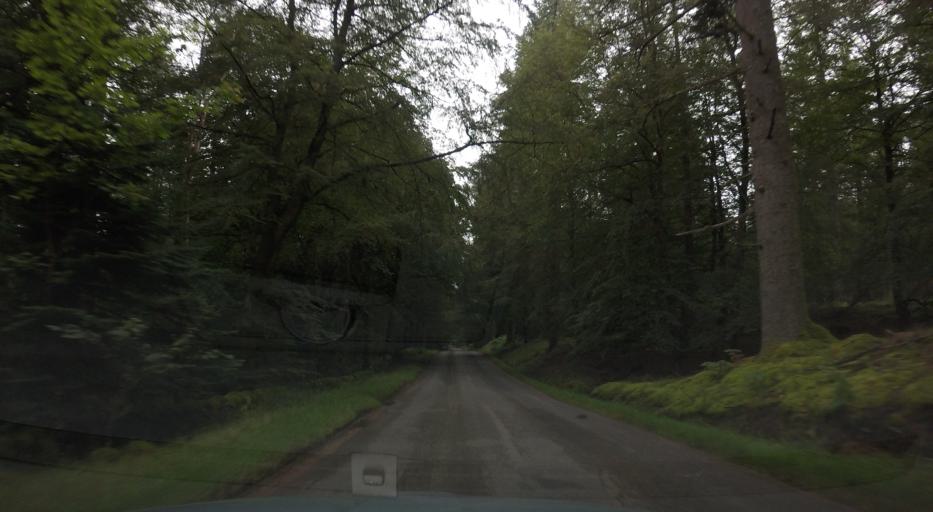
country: GB
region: Scotland
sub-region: Aberdeenshire
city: Banchory
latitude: 56.9743
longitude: -2.5764
